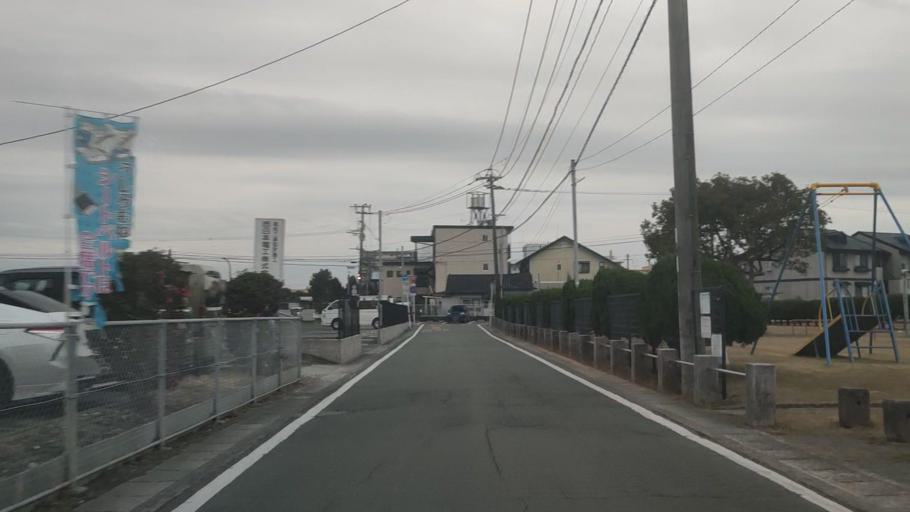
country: JP
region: Kumamoto
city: Kumamoto
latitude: 32.7664
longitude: 130.7099
